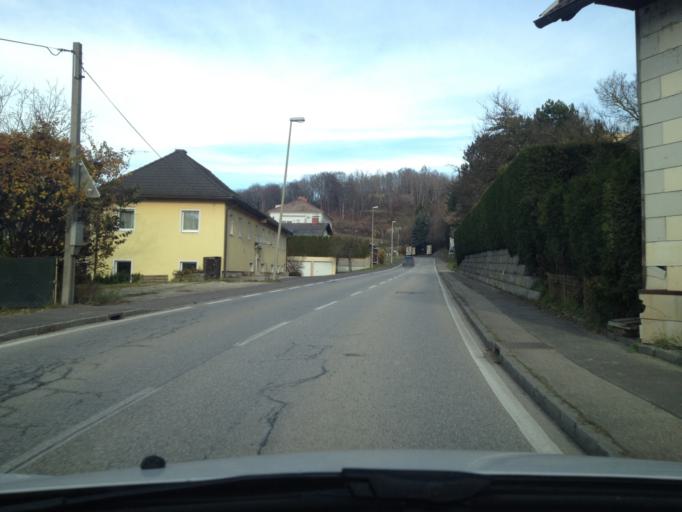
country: AT
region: Upper Austria
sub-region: Politischer Bezirk Urfahr-Umgebung
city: Steyregg
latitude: 48.3197
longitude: 14.3395
